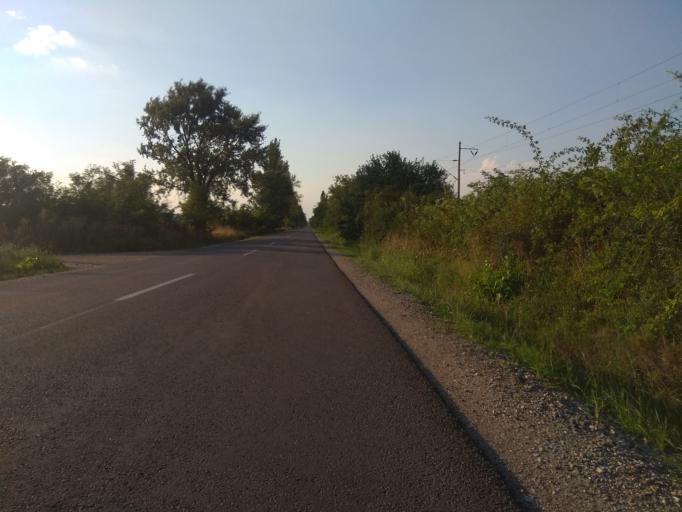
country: HU
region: Borsod-Abauj-Zemplen
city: Nyekladhaza
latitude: 47.9688
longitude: 20.8552
